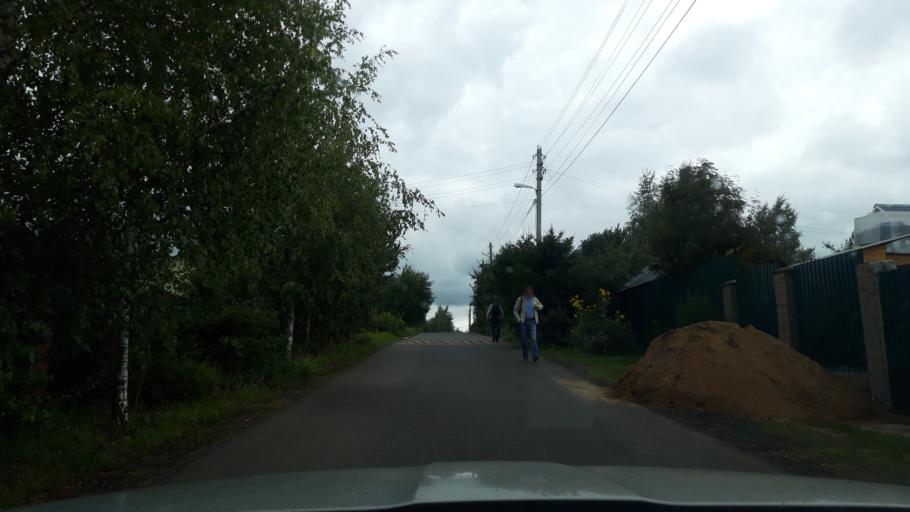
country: RU
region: Moskovskaya
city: Povarovo
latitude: 56.0977
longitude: 37.0671
